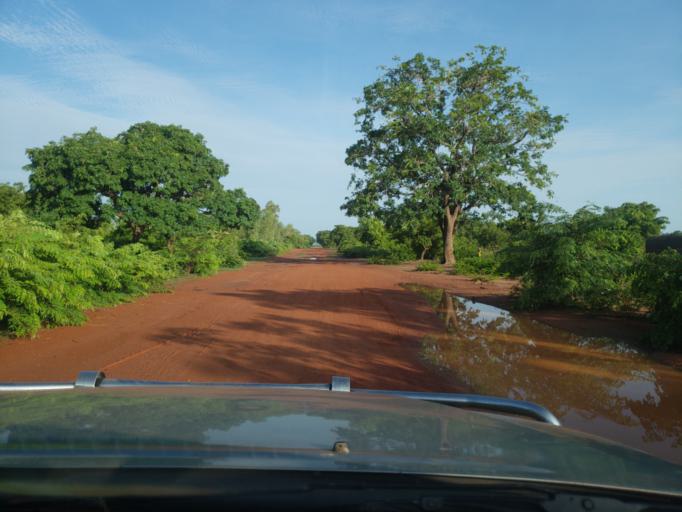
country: ML
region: Sikasso
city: Koutiala
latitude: 12.4266
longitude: -5.5984
